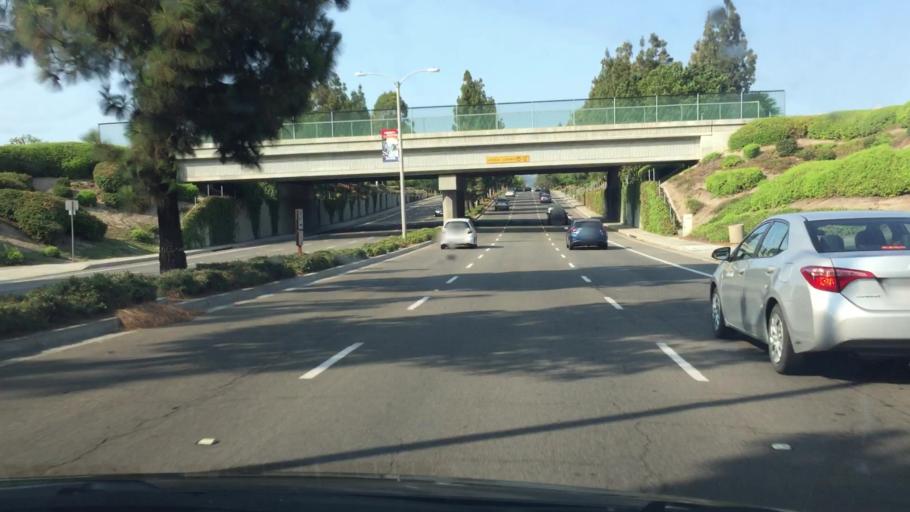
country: US
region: California
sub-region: Orange County
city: Irvine
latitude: 33.6986
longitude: -117.7937
